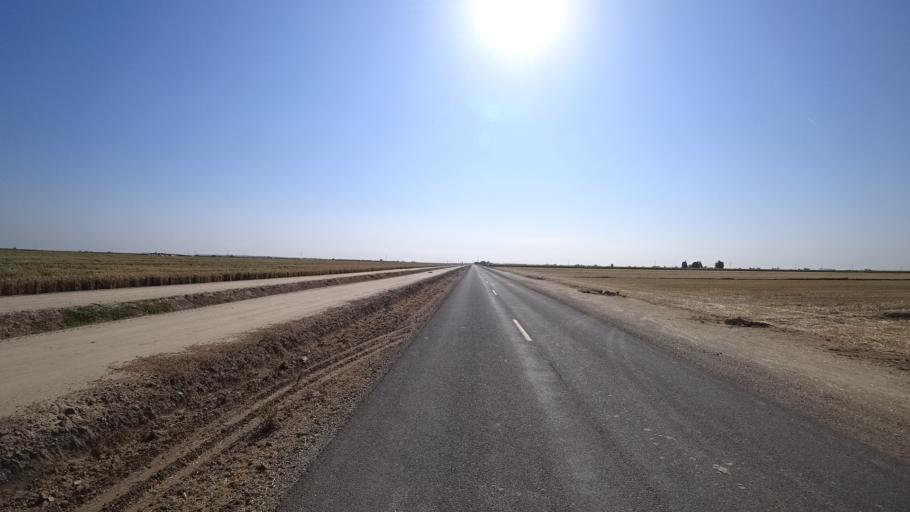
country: US
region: California
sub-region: Kings County
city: Home Garden
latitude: 36.2404
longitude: -119.5909
